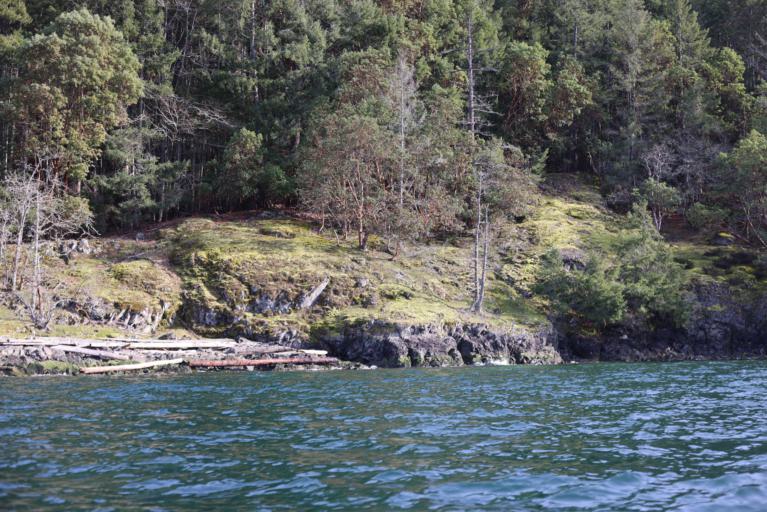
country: CA
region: British Columbia
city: Duncan
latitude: 48.7467
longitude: -123.5781
